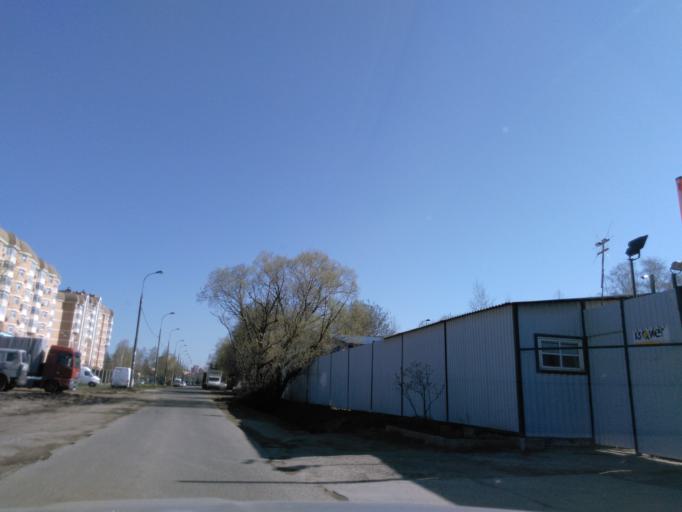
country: RU
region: Moscow
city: Khimki
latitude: 55.8827
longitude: 37.3903
